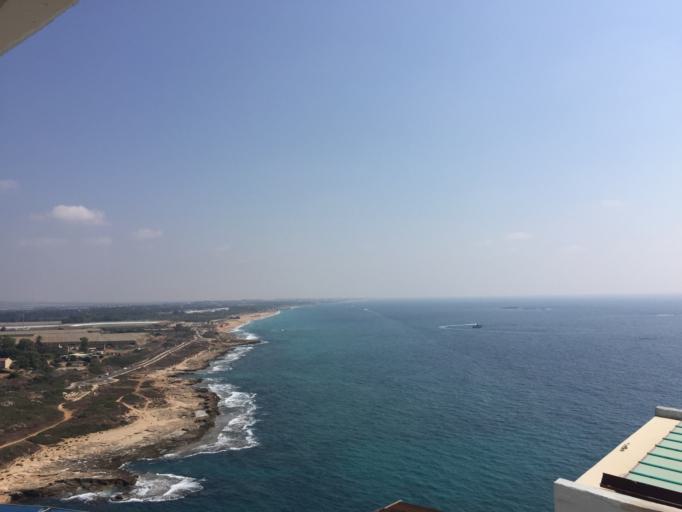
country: IL
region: Northern District
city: Kefar Rosh HaNiqra
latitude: 33.0931
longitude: 35.1050
